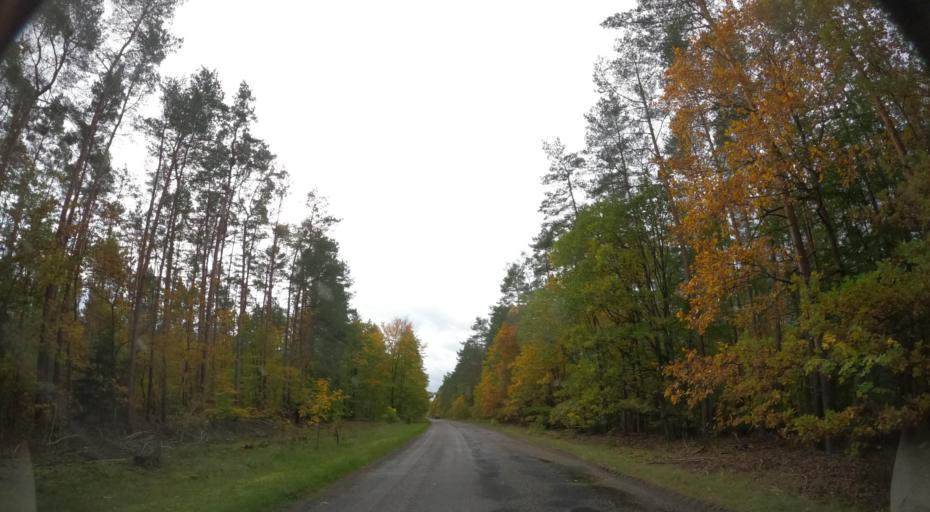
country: PL
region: West Pomeranian Voivodeship
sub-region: Powiat goleniowski
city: Stepnica
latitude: 53.6919
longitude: 14.6807
